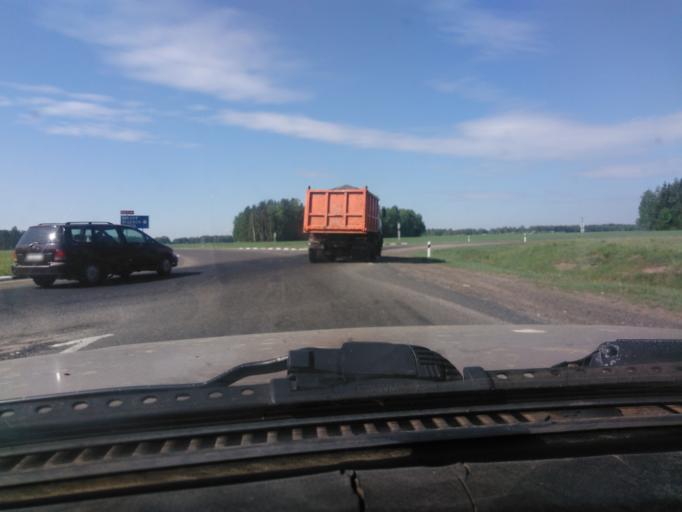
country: BY
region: Mogilev
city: Myazhysyatki
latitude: 53.8020
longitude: 30.2046
